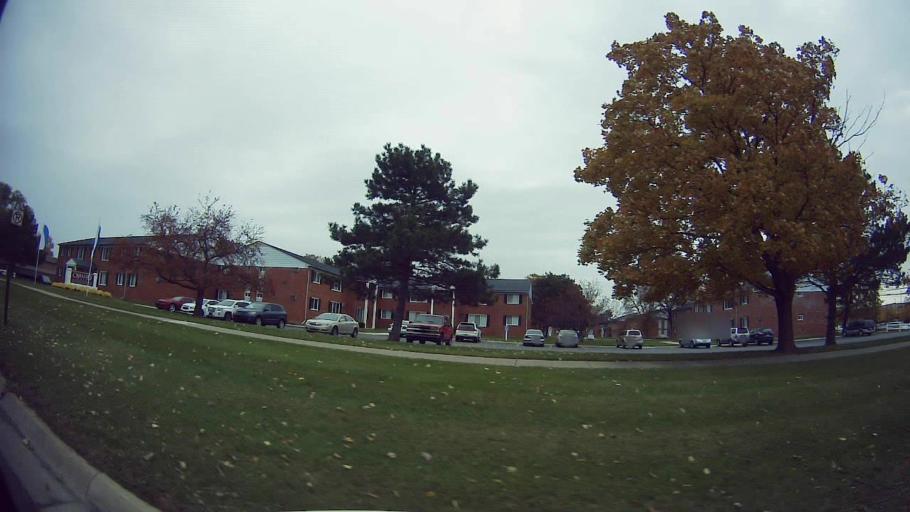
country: US
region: Michigan
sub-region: Oakland County
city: Madison Heights
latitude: 42.5230
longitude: -83.1064
